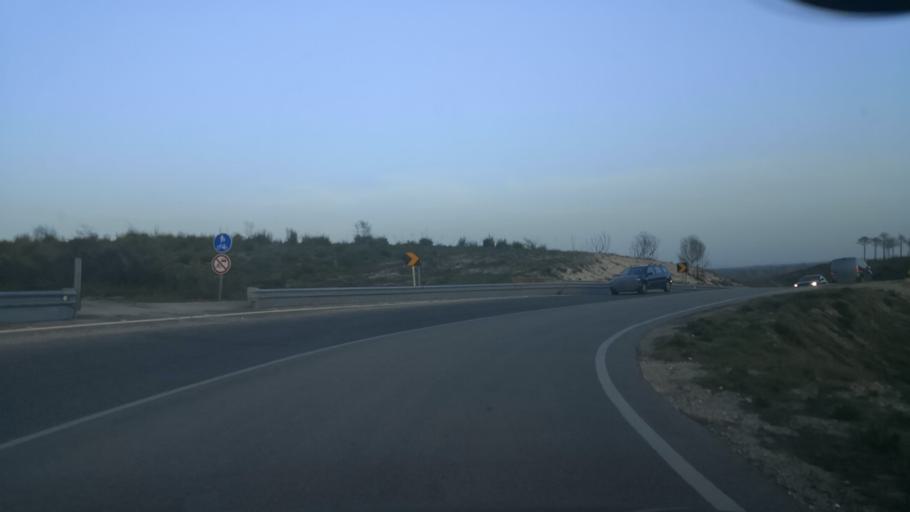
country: PT
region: Leiria
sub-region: Marinha Grande
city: Marinha Grande
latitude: 39.7461
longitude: -8.9883
